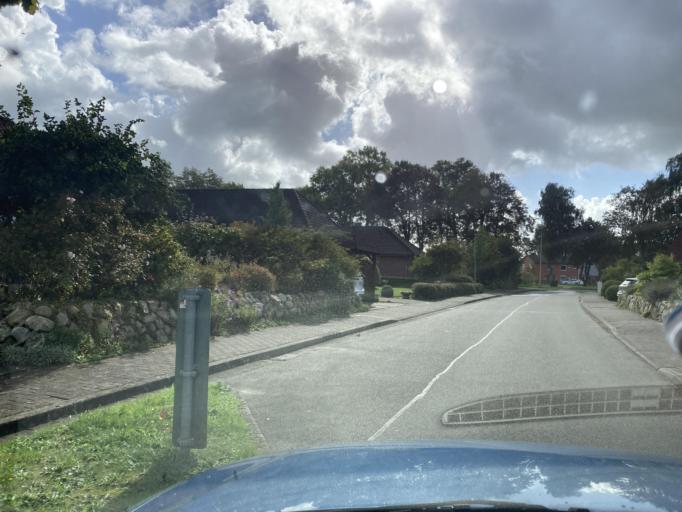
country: DE
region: Schleswig-Holstein
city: Wesseln
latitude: 54.2072
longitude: 9.0806
